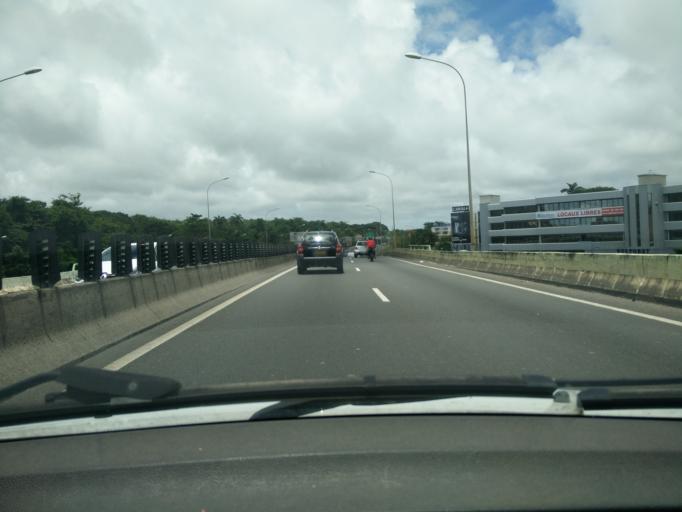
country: GP
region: Guadeloupe
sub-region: Guadeloupe
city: Pointe-a-Pitre
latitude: 16.2537
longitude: -61.5415
